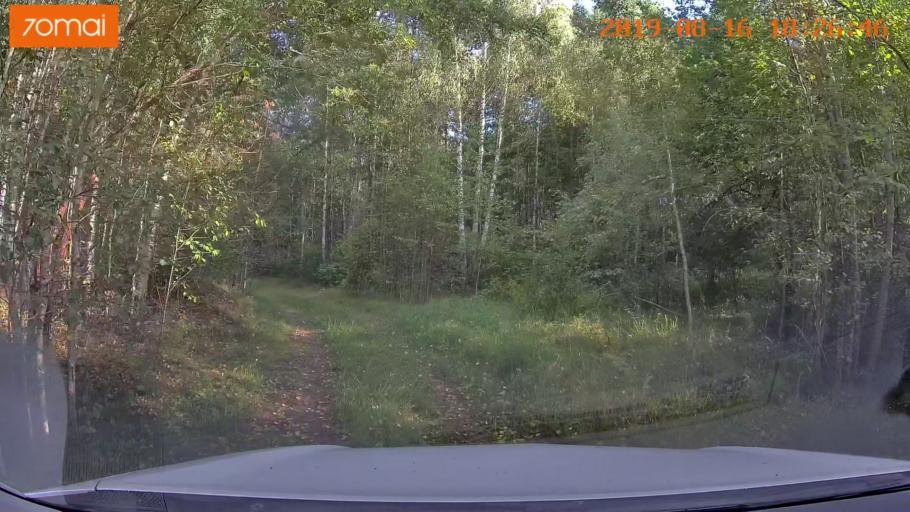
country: BY
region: Mogilev
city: Asipovichy
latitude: 53.2025
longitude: 28.6390
